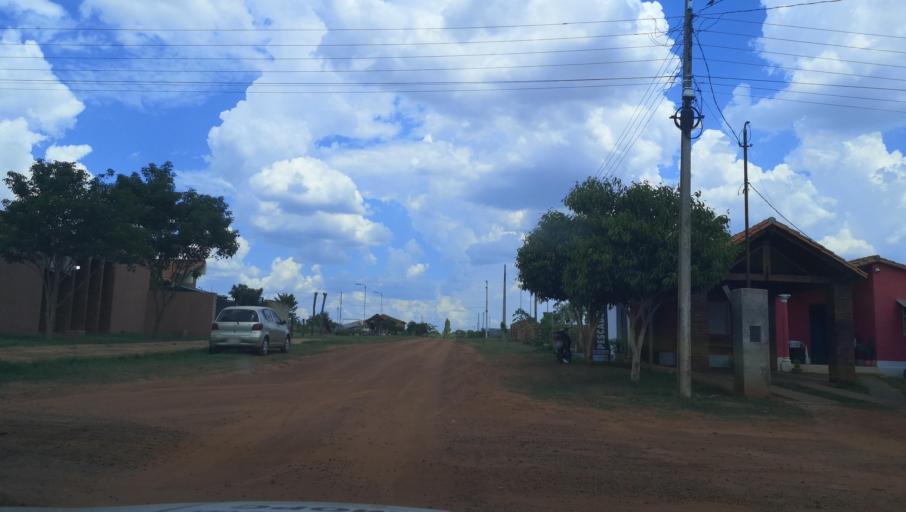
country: PY
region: Misiones
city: Santa Maria
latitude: -26.8925
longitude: -57.0388
